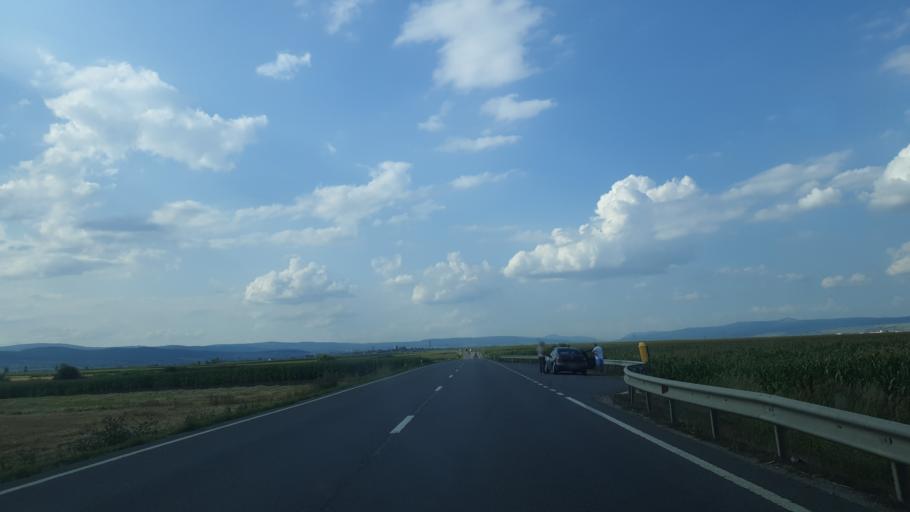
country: RO
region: Covasna
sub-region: Comuna Chichis
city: Chichis
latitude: 45.7869
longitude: 25.8071
